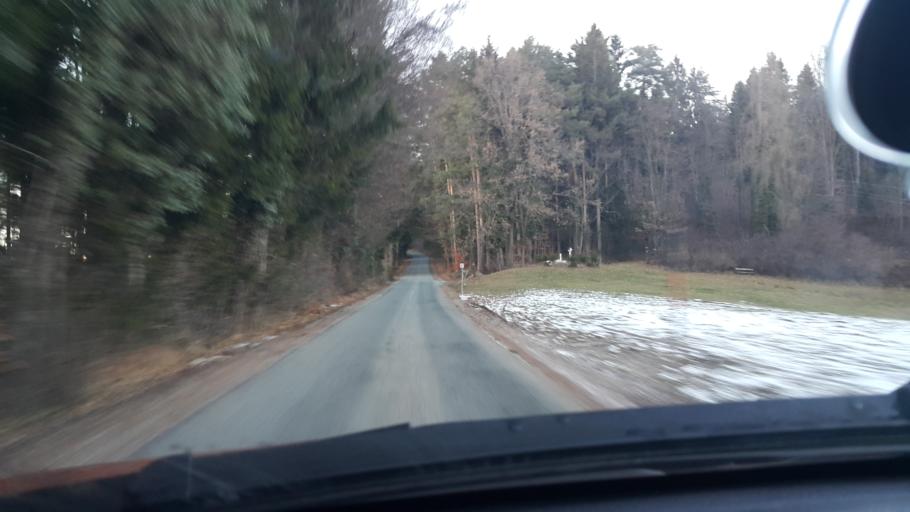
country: AT
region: Styria
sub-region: Politischer Bezirk Graz-Umgebung
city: Stiwoll
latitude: 47.1150
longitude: 15.2184
